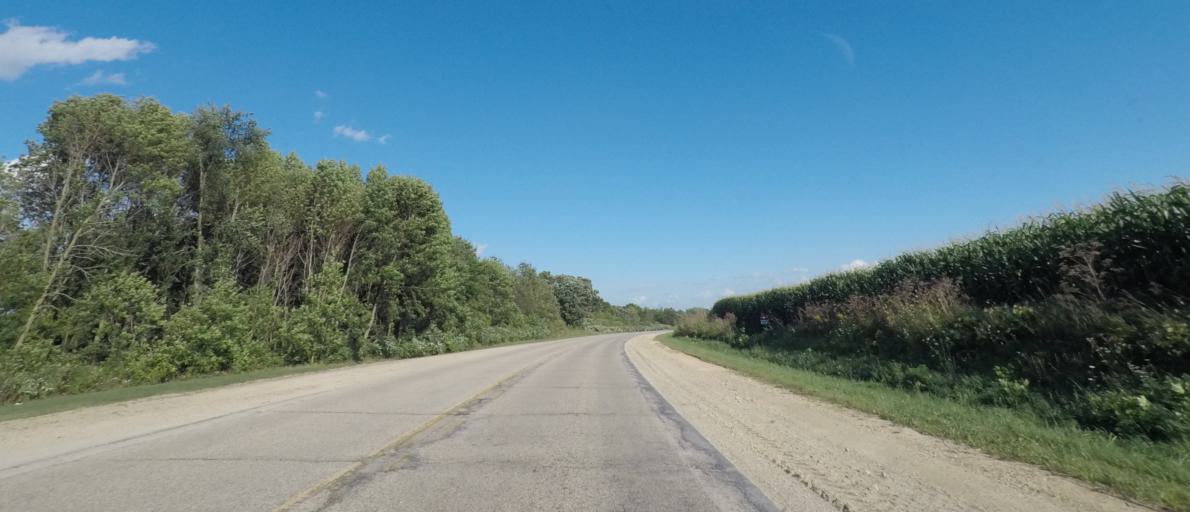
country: US
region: Wisconsin
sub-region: Iowa County
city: Dodgeville
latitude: 42.9794
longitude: -90.0590
